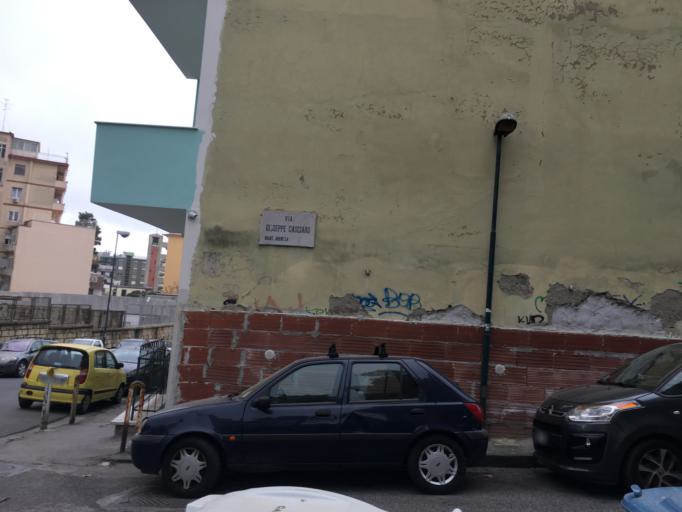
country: IT
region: Campania
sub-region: Provincia di Napoli
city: Napoli
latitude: 40.8546
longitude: 14.2238
